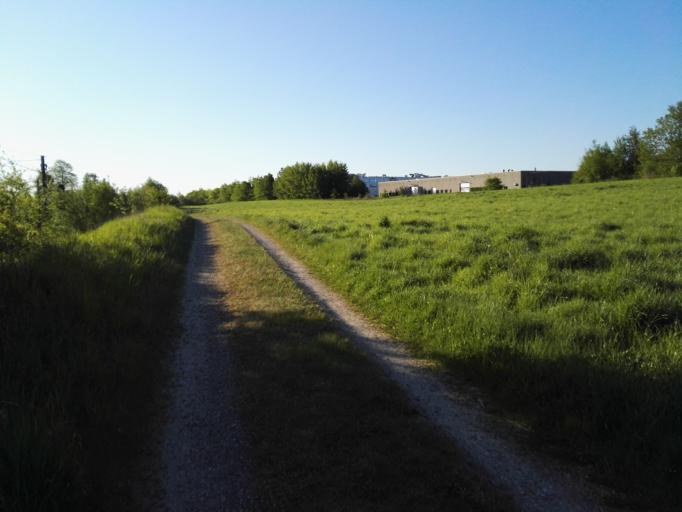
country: DK
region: Capital Region
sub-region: Ballerup Kommune
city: Ballerup
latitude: 55.7360
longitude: 12.3432
